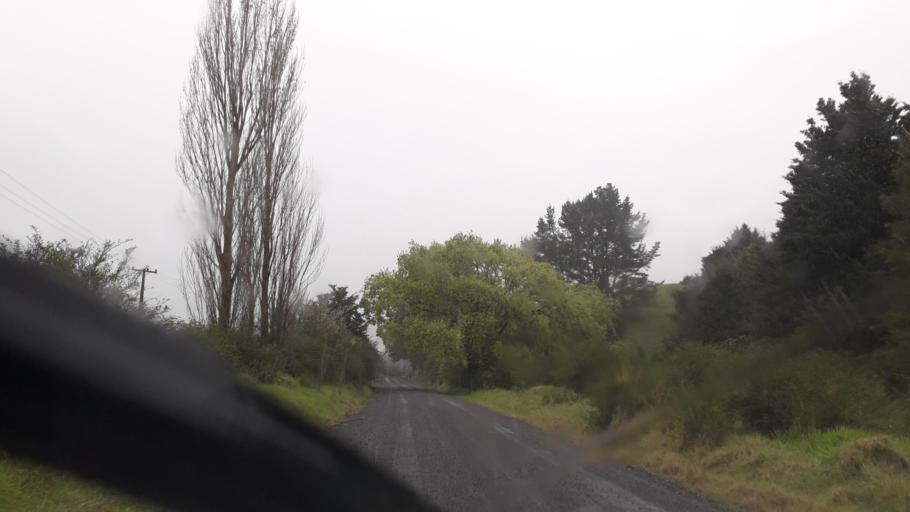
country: NZ
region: Northland
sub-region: Far North District
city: Waimate North
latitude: -35.4871
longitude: 173.7009
